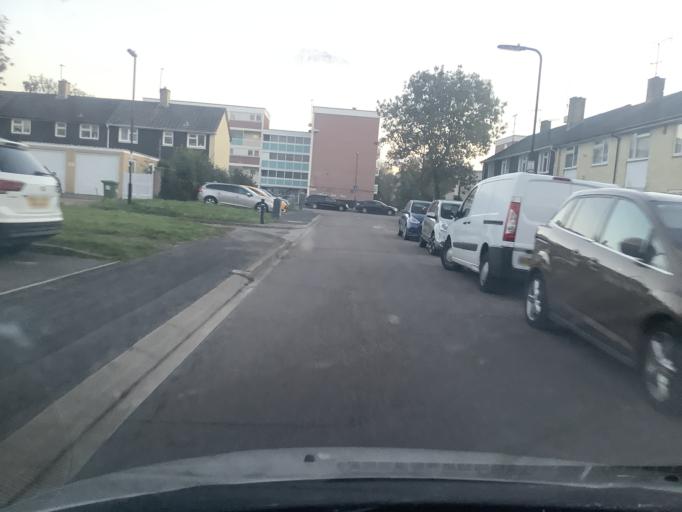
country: GB
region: England
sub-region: Hampshire
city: Marchwood
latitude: 50.9281
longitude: -1.4490
